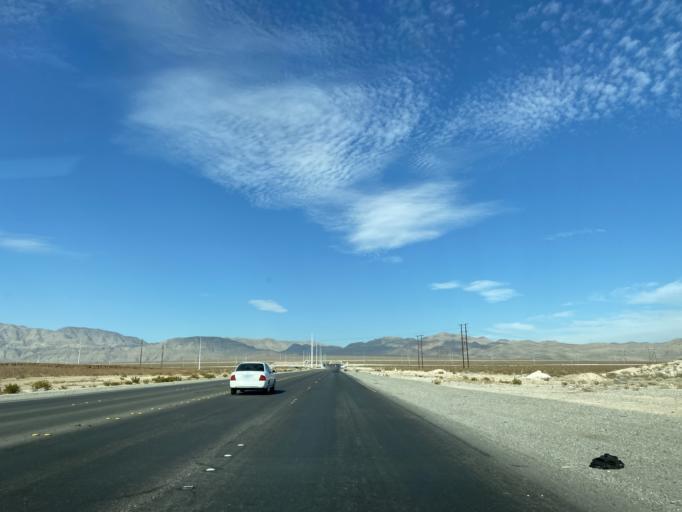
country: US
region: Nevada
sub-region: Clark County
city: Nellis Air Force Base
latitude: 36.2785
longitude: -115.0799
